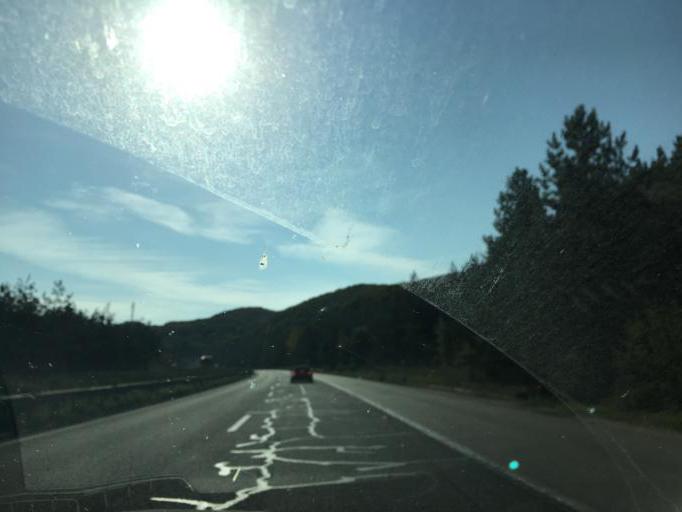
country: BG
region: Sofiya
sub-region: Obshtina Ikhtiman
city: Ikhtiman
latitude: 42.3566
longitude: 23.9110
